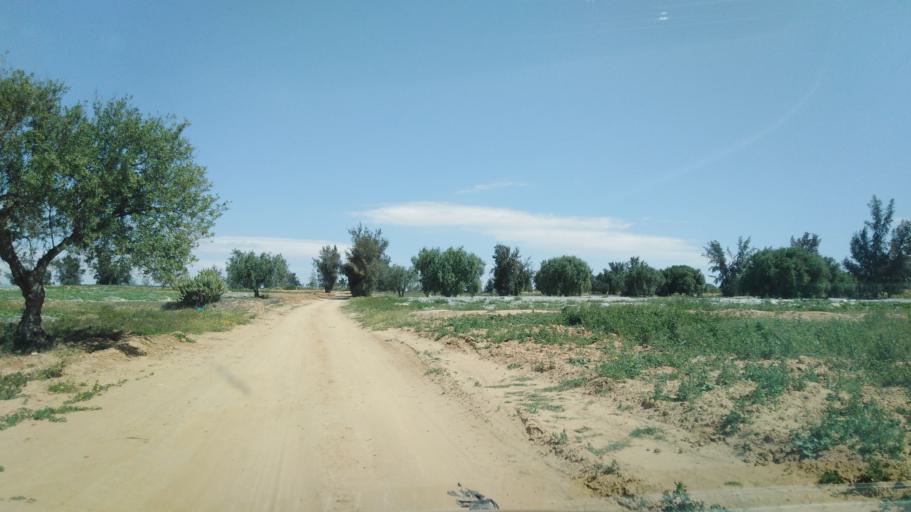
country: TN
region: Safaqis
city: Sfax
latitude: 34.7698
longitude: 10.5278
